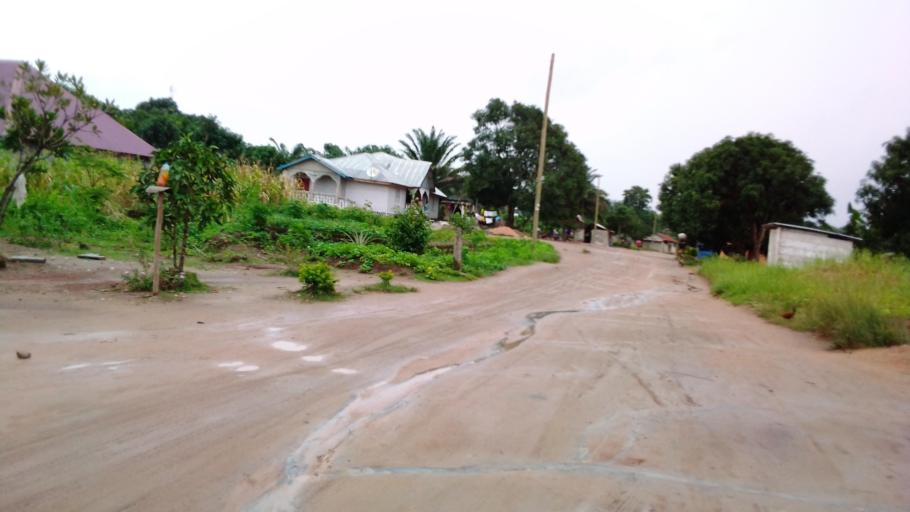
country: SL
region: Eastern Province
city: Kenema
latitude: 7.8617
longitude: -11.1712
